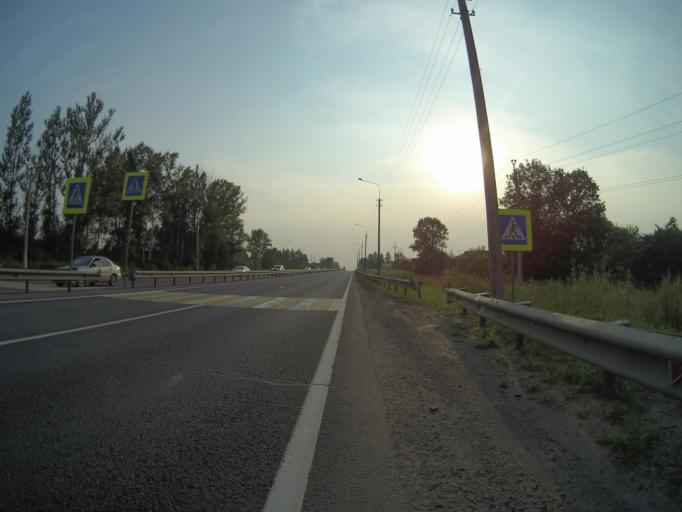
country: RU
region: Vladimir
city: Novki
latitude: 56.2021
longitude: 41.1089
